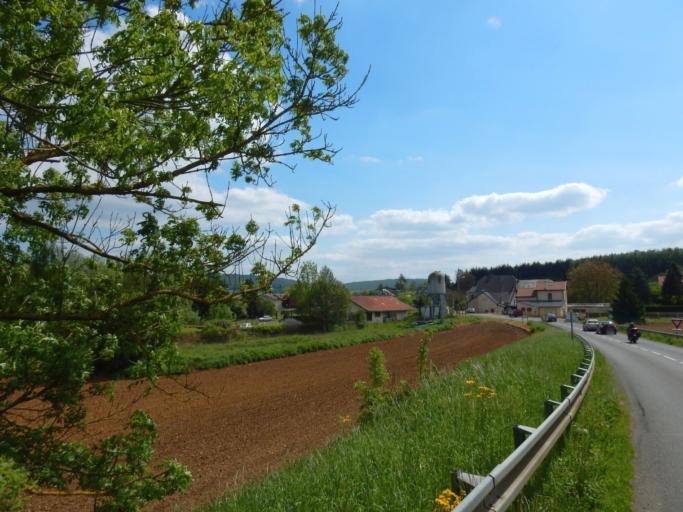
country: FR
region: Champagne-Ardenne
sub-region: Departement des Ardennes
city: Bazeilles
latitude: 49.6595
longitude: 4.9849
